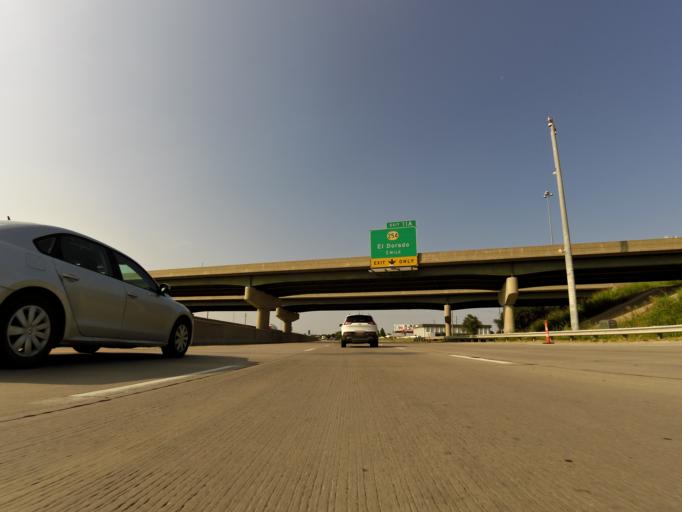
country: US
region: Kansas
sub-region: Sedgwick County
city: Wichita
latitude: 37.7433
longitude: -97.3189
